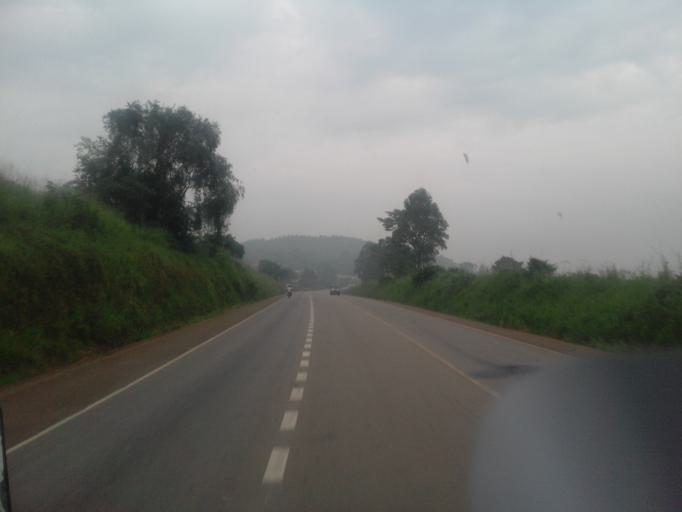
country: UG
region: Central Region
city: Lugazi
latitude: 0.3714
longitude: 32.8929
